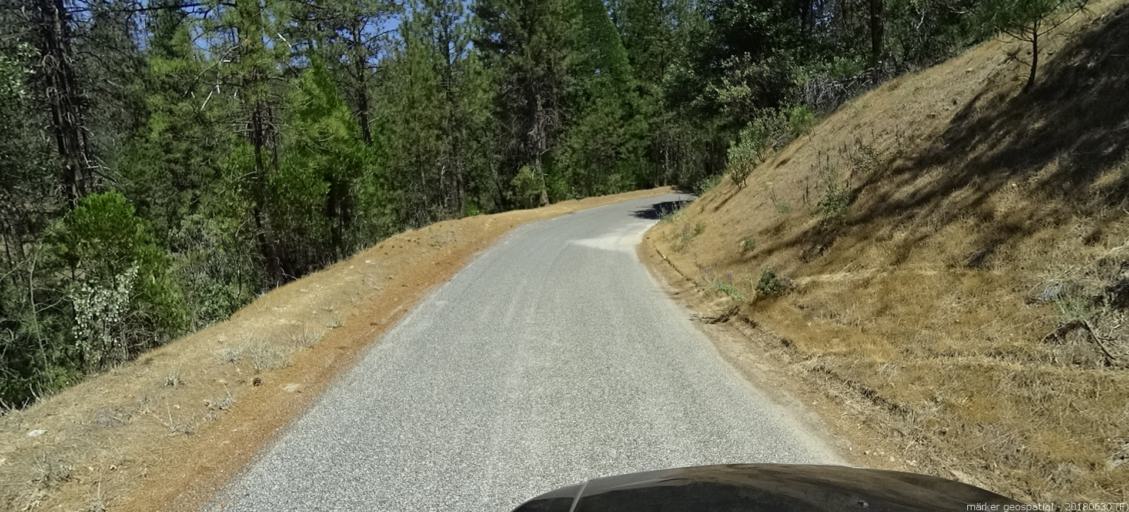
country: US
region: California
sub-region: Madera County
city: Oakhurst
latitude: 37.3635
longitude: -119.3521
